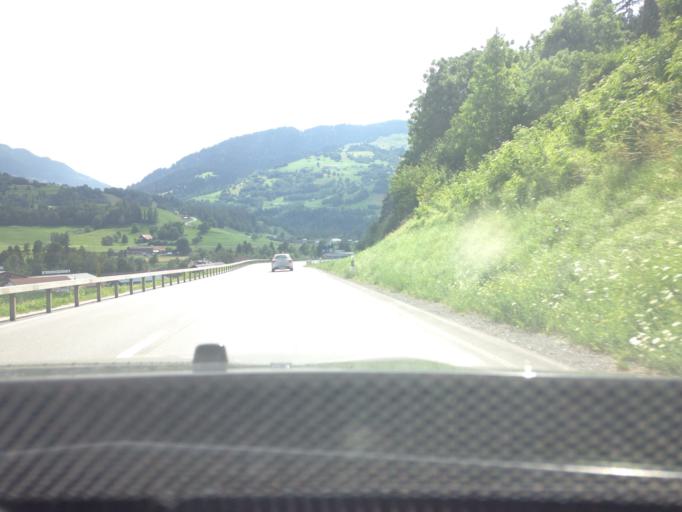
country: CH
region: Grisons
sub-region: Surselva District
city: Ilanz
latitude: 46.7817
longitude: 9.2203
